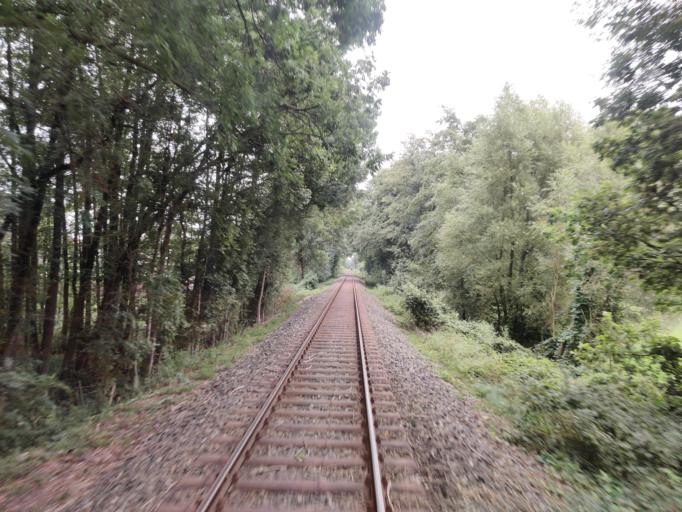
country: DE
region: Lower Saxony
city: Deinste
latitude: 53.5287
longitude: 9.4393
